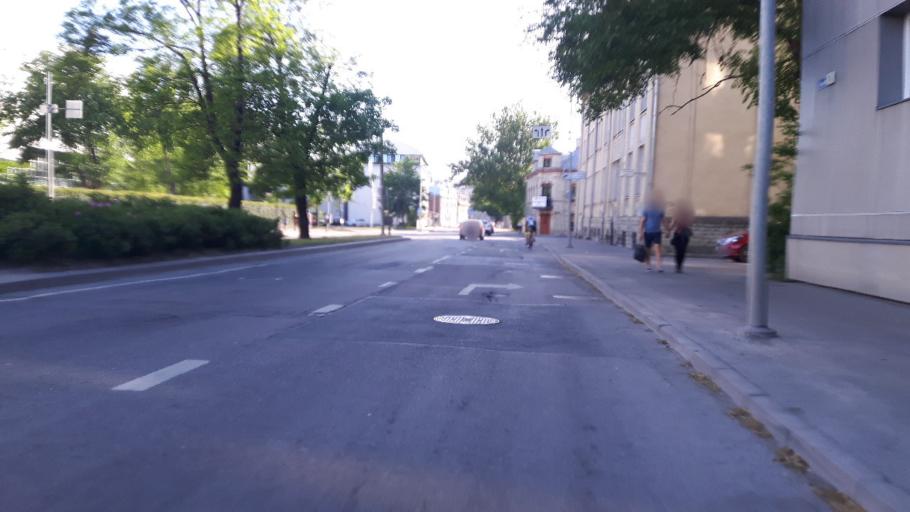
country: EE
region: Harju
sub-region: Tallinna linn
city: Tallinn
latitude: 59.4405
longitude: 24.7739
